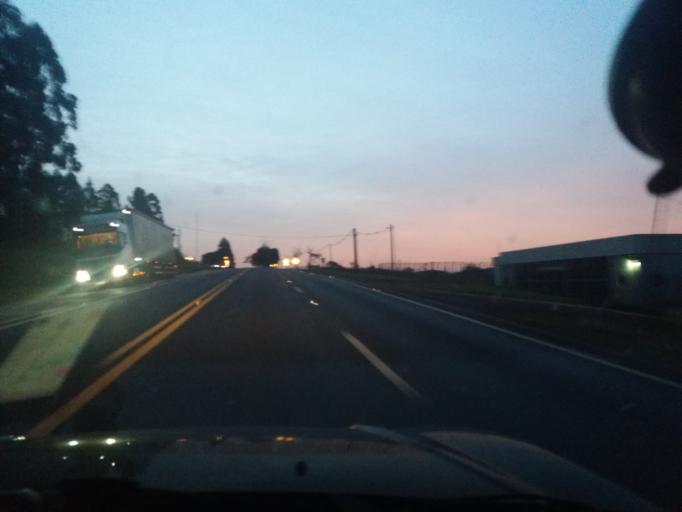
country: BR
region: Sao Paulo
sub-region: Itapeva
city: Itapeva
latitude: -23.9750
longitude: -48.8563
